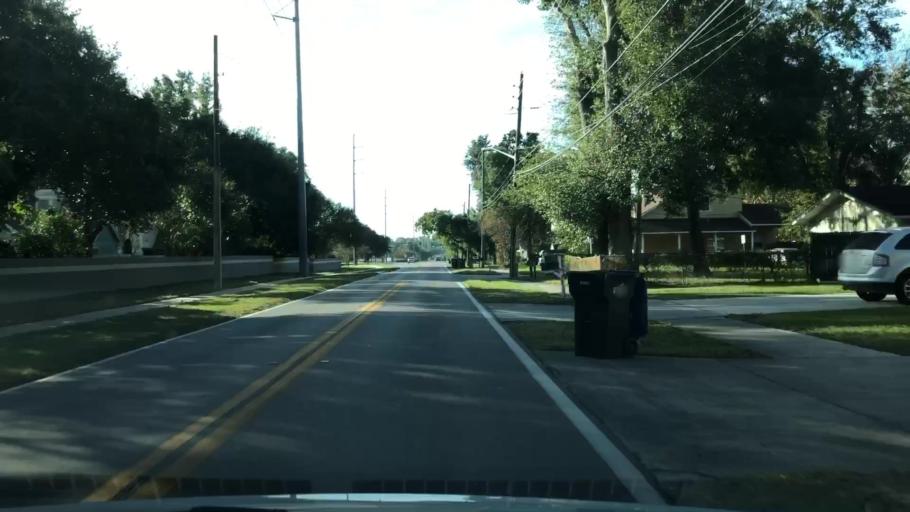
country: US
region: Florida
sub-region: Orange County
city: Conway
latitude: 28.5157
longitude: -81.3393
